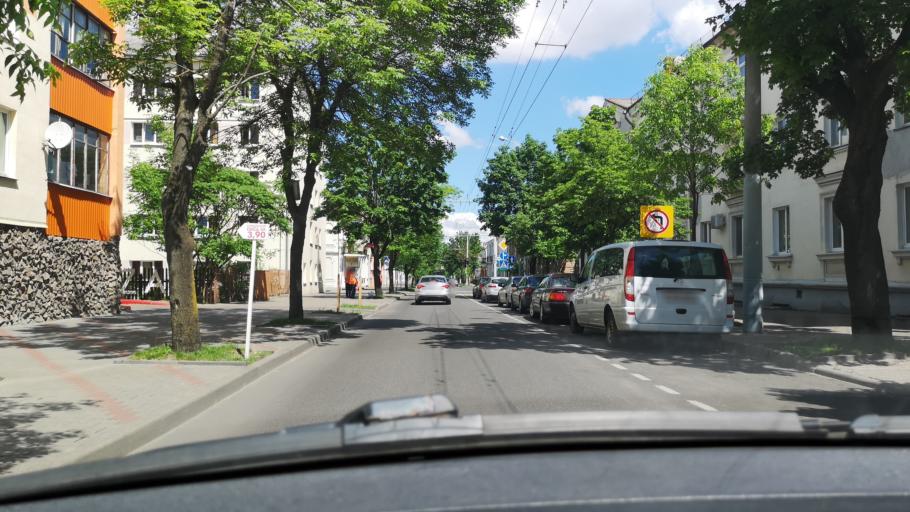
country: BY
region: Brest
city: Brest
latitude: 52.0877
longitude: 23.6890
